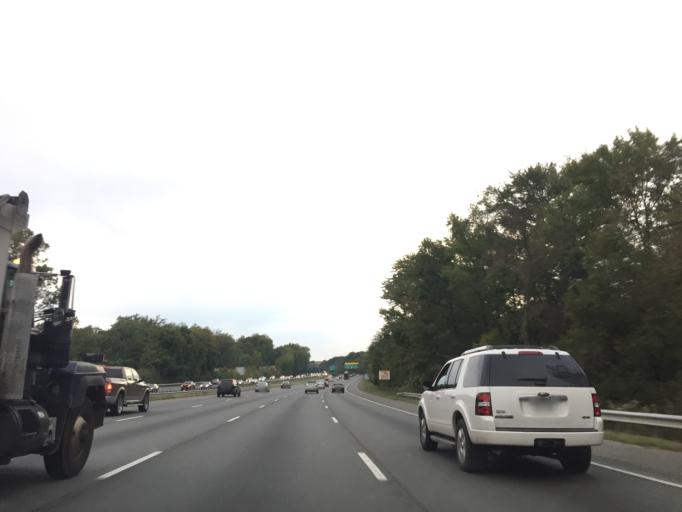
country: US
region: Maryland
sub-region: Prince George's County
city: Temple Hills
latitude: 38.8180
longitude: -76.9368
